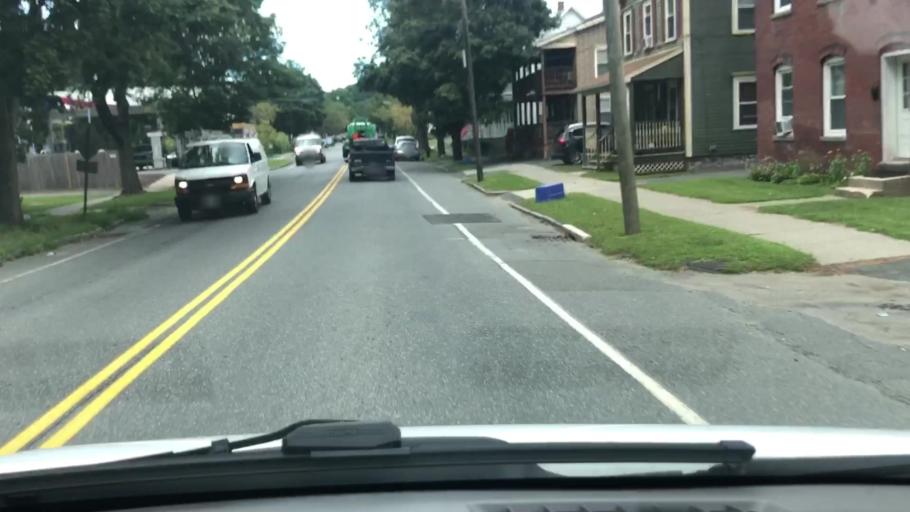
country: US
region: Massachusetts
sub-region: Franklin County
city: Turners Falls
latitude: 42.6065
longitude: -72.5538
